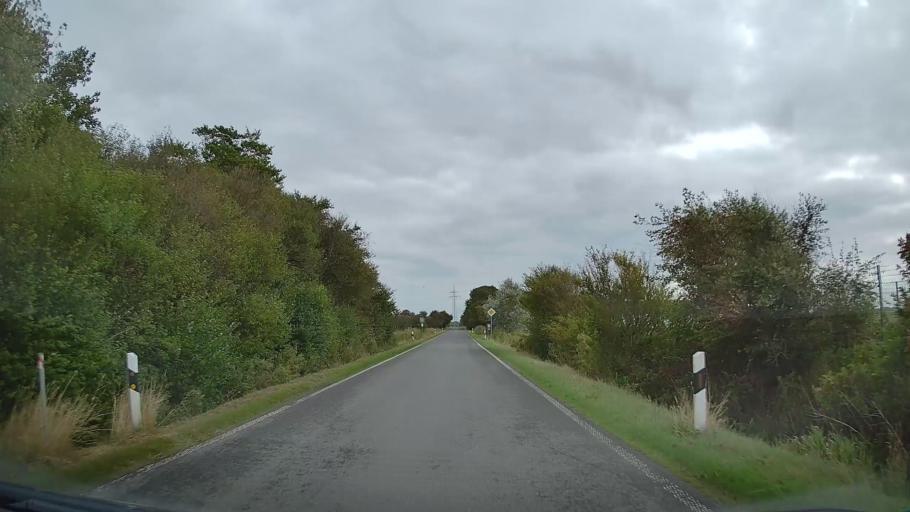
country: DE
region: Schleswig-Holstein
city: Friedrich-Wilhelm-Lubke-Koog
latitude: 54.8676
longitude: 8.6510
